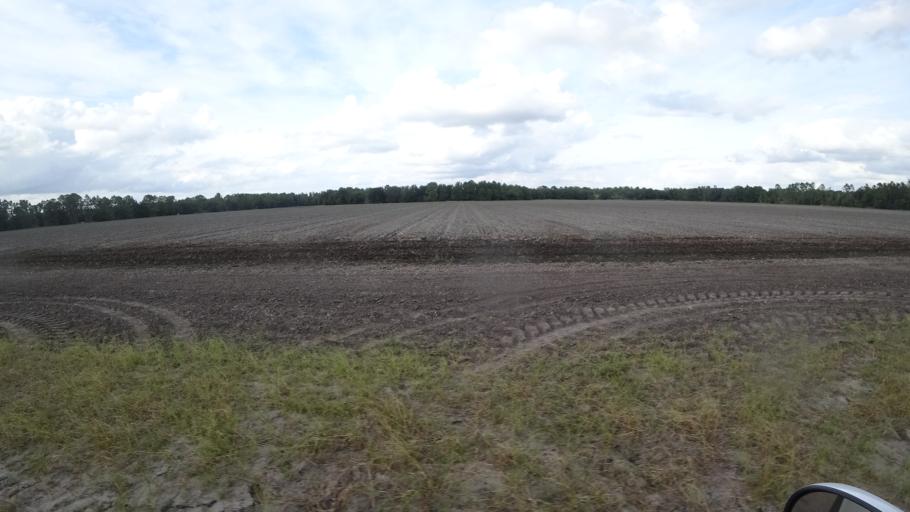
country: US
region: Florida
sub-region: Hillsborough County
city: Balm
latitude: 27.6235
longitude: -82.1260
